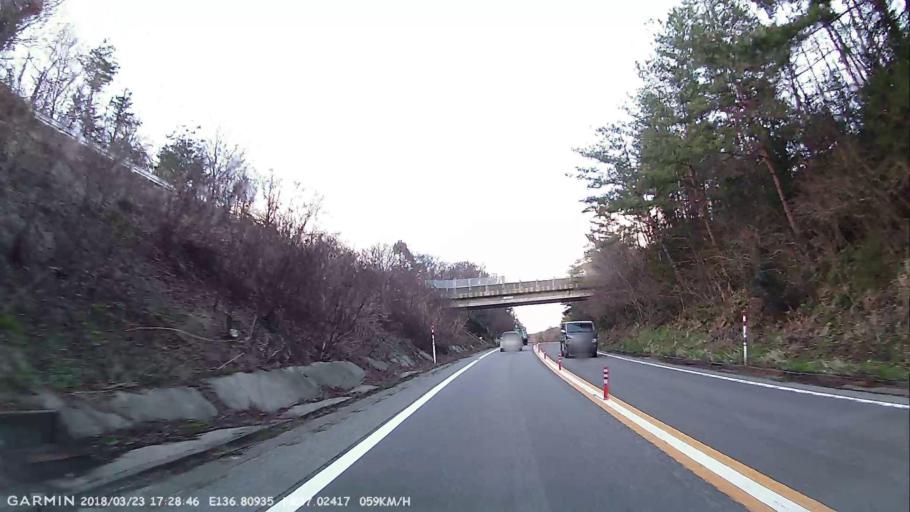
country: JP
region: Ishikawa
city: Hakui
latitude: 37.0244
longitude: 136.8095
